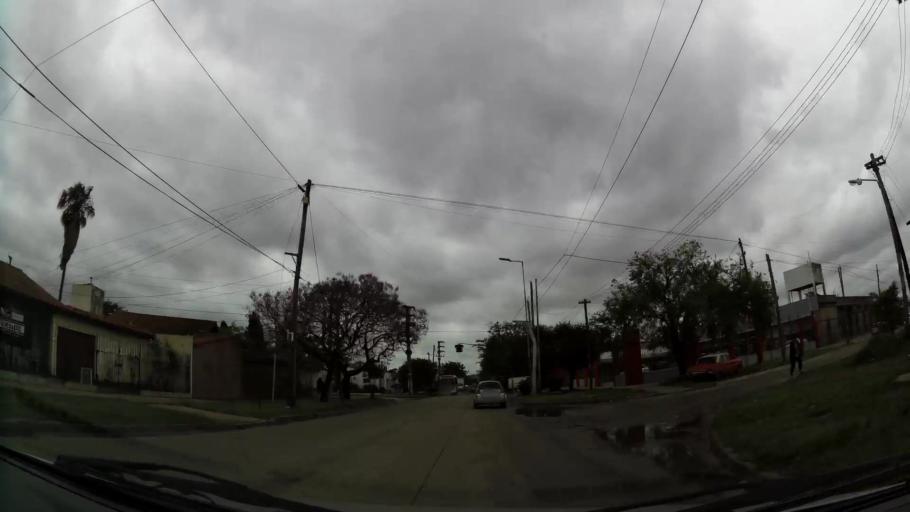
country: AR
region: Buenos Aires
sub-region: Partido de Lomas de Zamora
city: Lomas de Zamora
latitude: -34.7488
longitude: -58.3707
